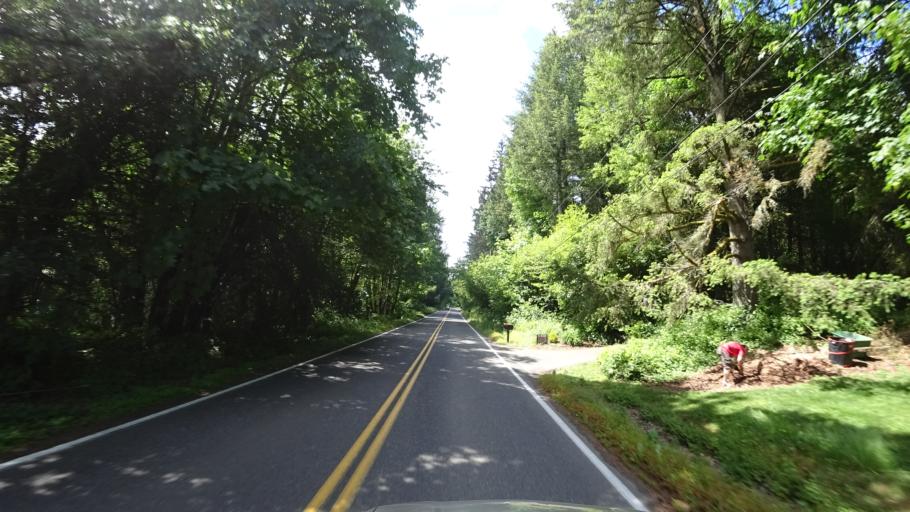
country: US
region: Oregon
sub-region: Washington County
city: Oak Hills
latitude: 45.5845
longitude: -122.8023
